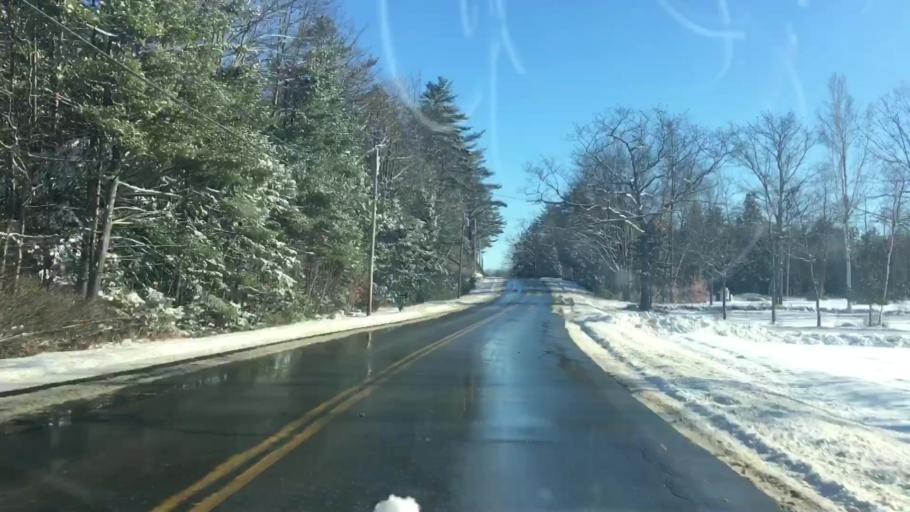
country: US
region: Maine
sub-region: Androscoggin County
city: Lisbon Falls
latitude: 43.9326
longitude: -70.0551
